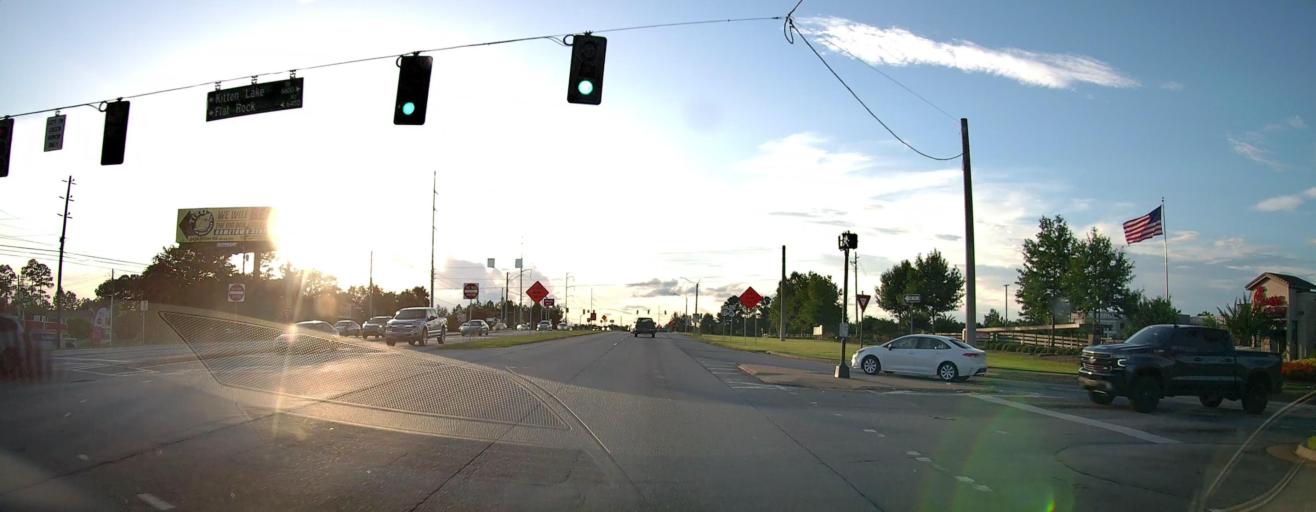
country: US
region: Georgia
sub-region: Muscogee County
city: Columbus
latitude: 32.5389
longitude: -84.8700
